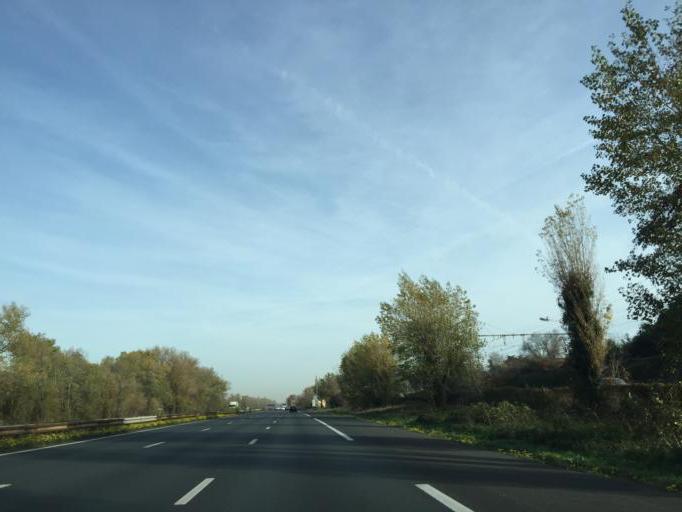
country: FR
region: Rhone-Alpes
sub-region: Departement du Rhone
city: Ternay
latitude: 45.6195
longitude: 4.8127
